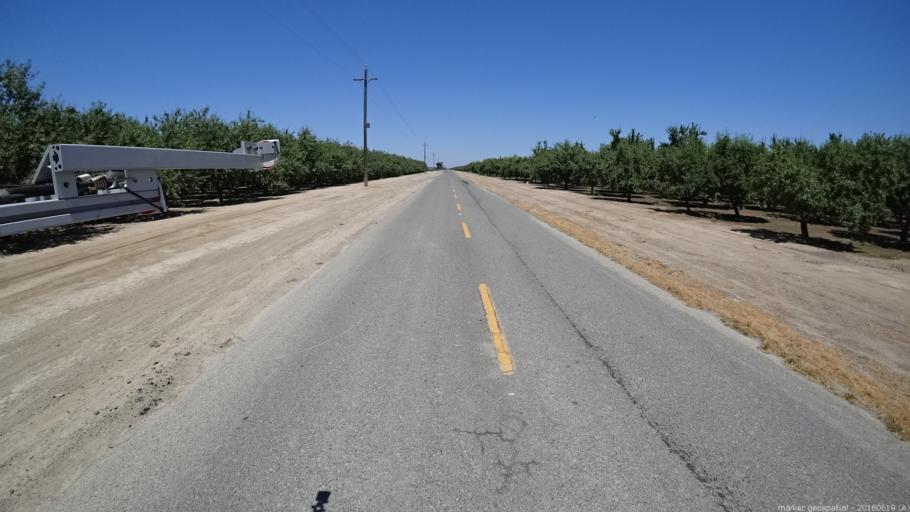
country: US
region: California
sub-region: Madera County
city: Parkwood
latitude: 36.8563
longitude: -120.1647
